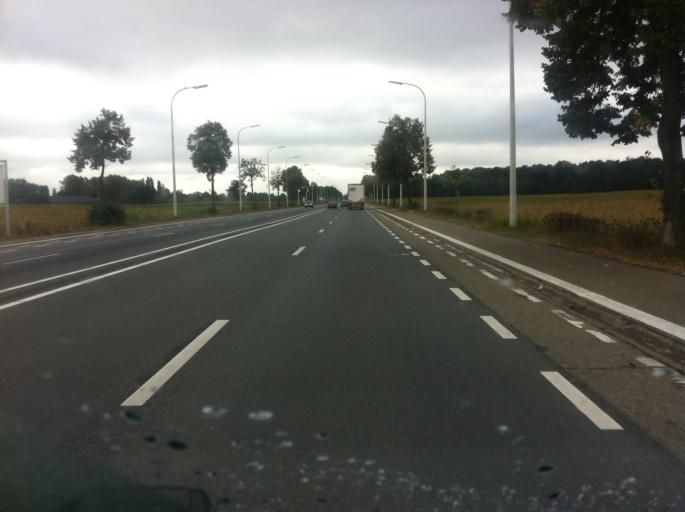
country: BE
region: Flanders
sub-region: Provincie Limburg
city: Maasmechelen
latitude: 50.9362
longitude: 5.6910
